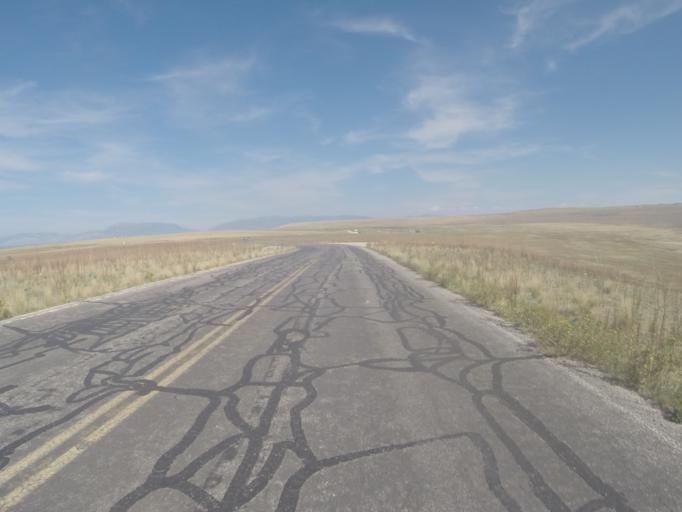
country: US
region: Utah
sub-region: Weber County
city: Hooper
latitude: 41.0350
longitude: -112.2481
